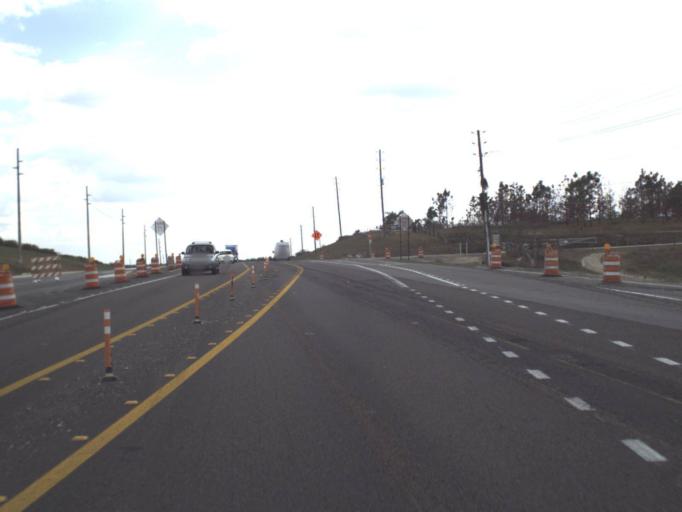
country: US
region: Florida
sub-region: Lake County
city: Clermont
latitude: 28.4579
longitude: -81.7206
